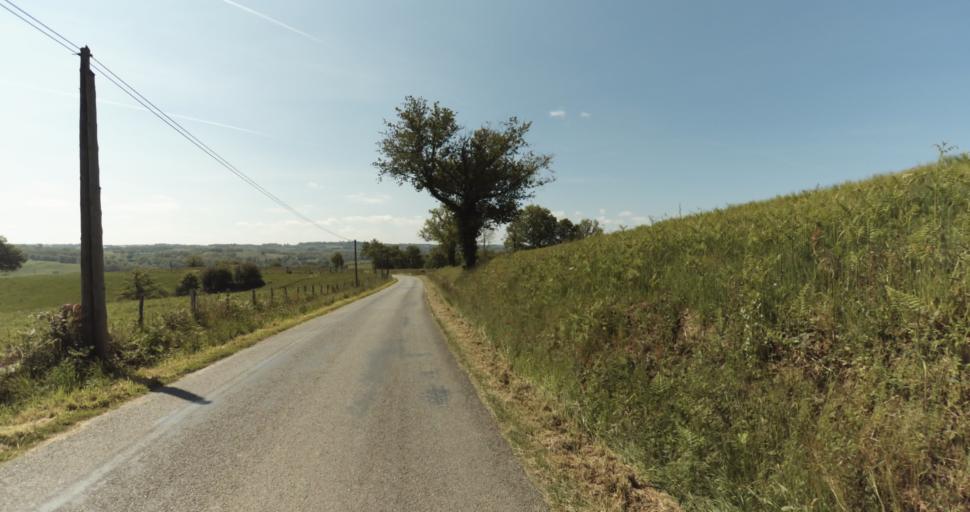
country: FR
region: Limousin
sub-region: Departement de la Haute-Vienne
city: Le Vigen
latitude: 45.7091
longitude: 1.2987
